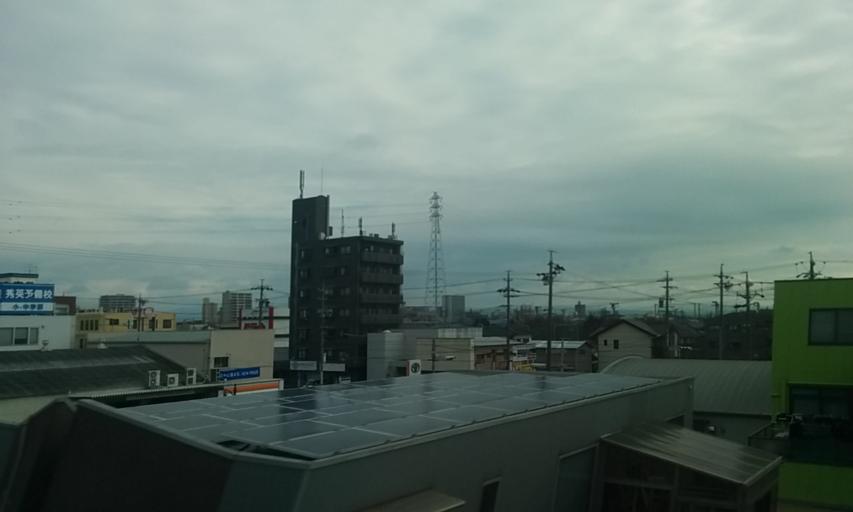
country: JP
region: Aichi
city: Anjo
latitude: 34.9514
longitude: 137.0766
